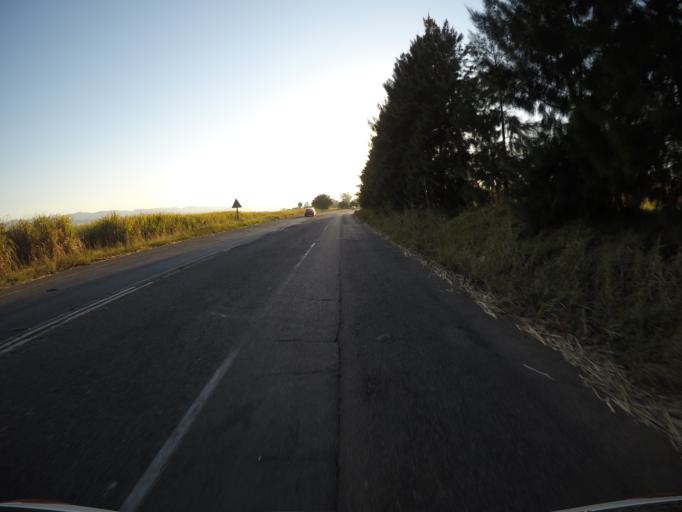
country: ZA
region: KwaZulu-Natal
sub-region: uThungulu District Municipality
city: Eshowe
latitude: -28.9474
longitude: 31.6790
